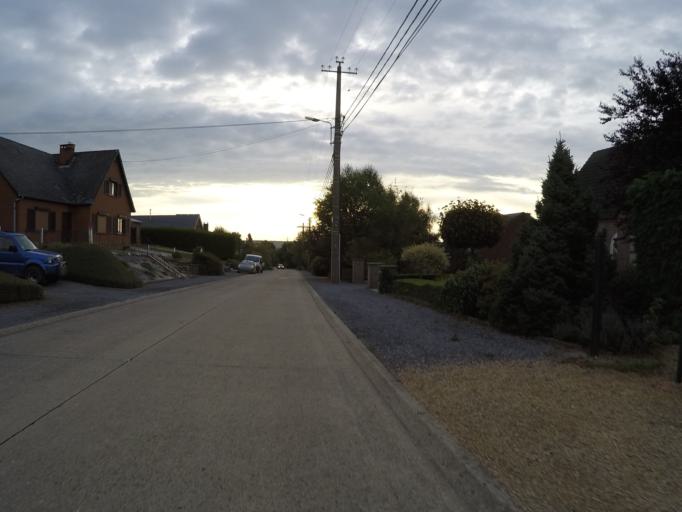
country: BE
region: Wallonia
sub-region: Province de Namur
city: Assesse
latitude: 50.3381
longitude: 5.0496
